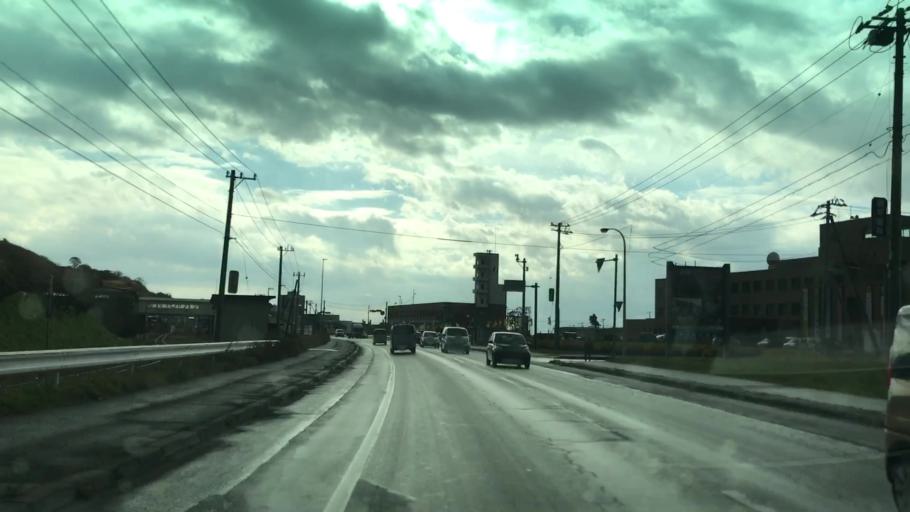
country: JP
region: Hokkaido
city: Shizunai-furukawacho
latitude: 42.1698
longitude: 142.7683
